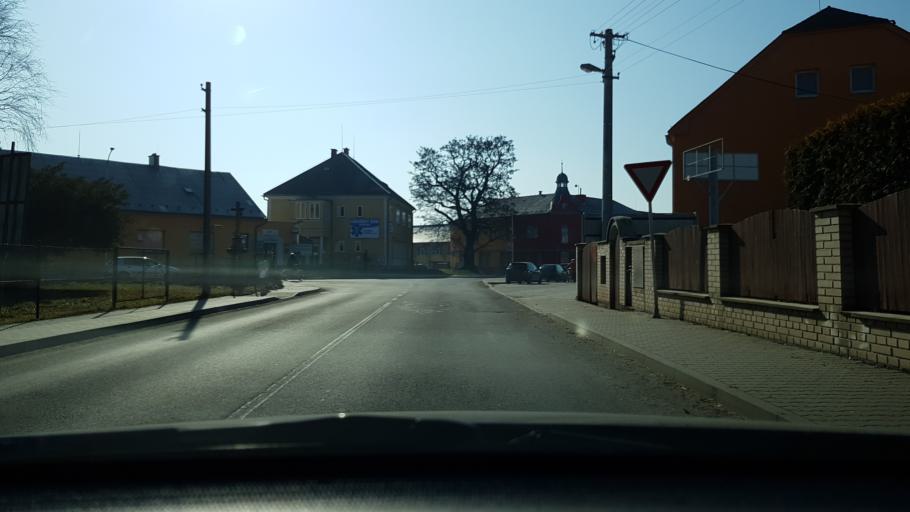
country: CZ
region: Olomoucky
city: Postrelmov
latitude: 49.9097
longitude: 16.9132
